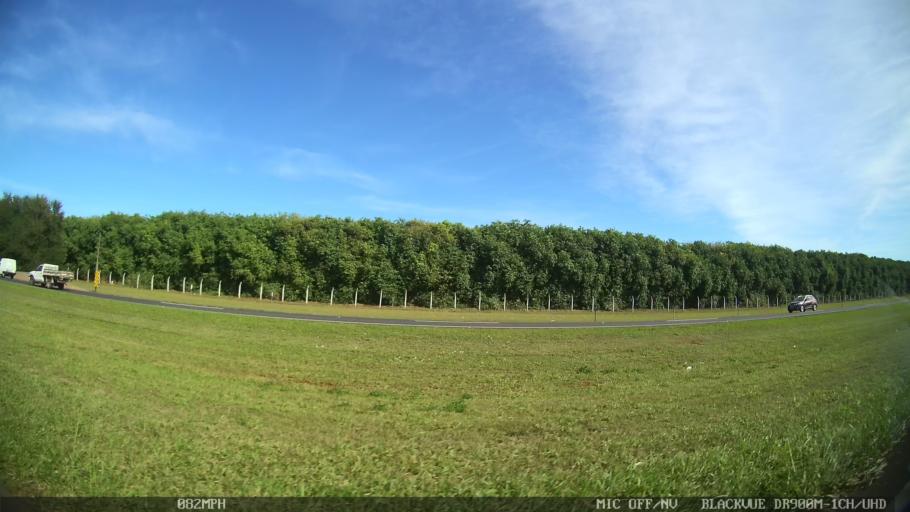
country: BR
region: Sao Paulo
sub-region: Cordeiropolis
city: Cordeiropolis
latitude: -22.4549
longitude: -47.3987
